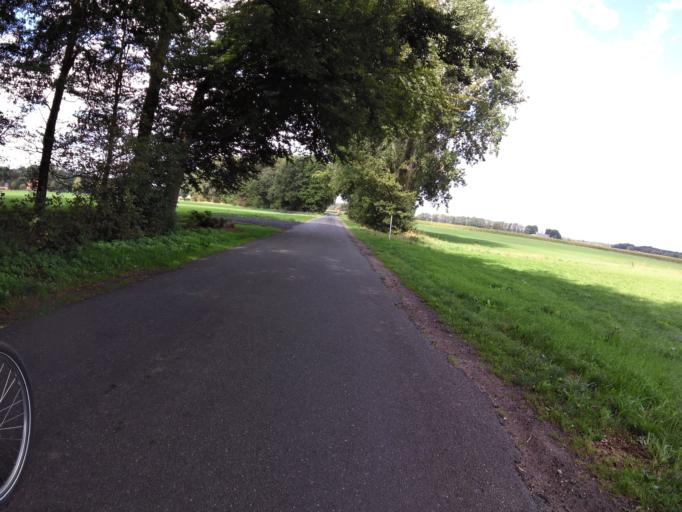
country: DE
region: North Rhine-Westphalia
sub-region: Regierungsbezirk Munster
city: Gronau
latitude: 52.1527
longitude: 7.0461
